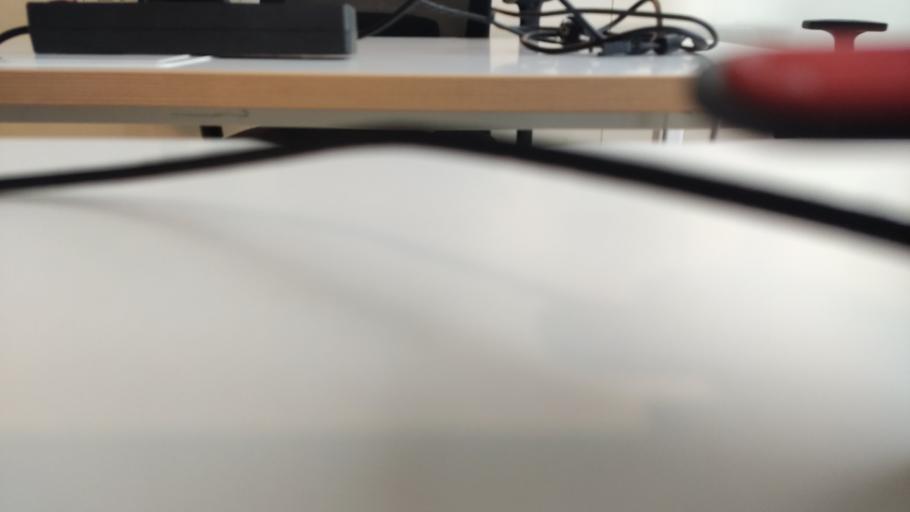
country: RU
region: Moskovskaya
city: Rogachevo
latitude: 56.4108
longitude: 37.0575
